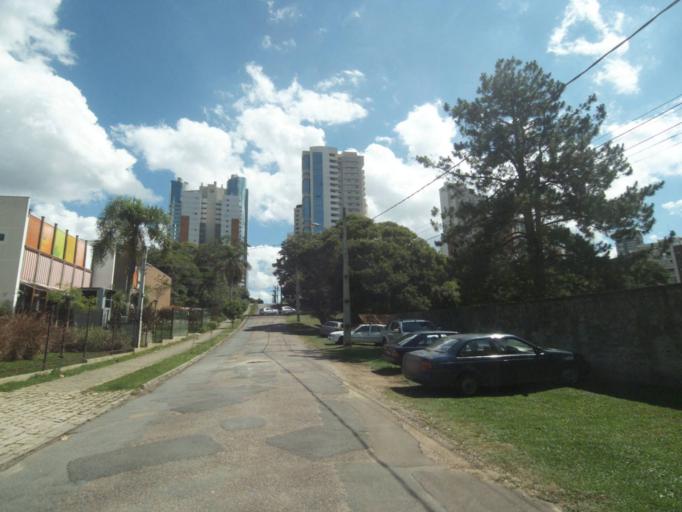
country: BR
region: Parana
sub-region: Curitiba
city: Curitiba
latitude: -25.4373
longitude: -49.3370
